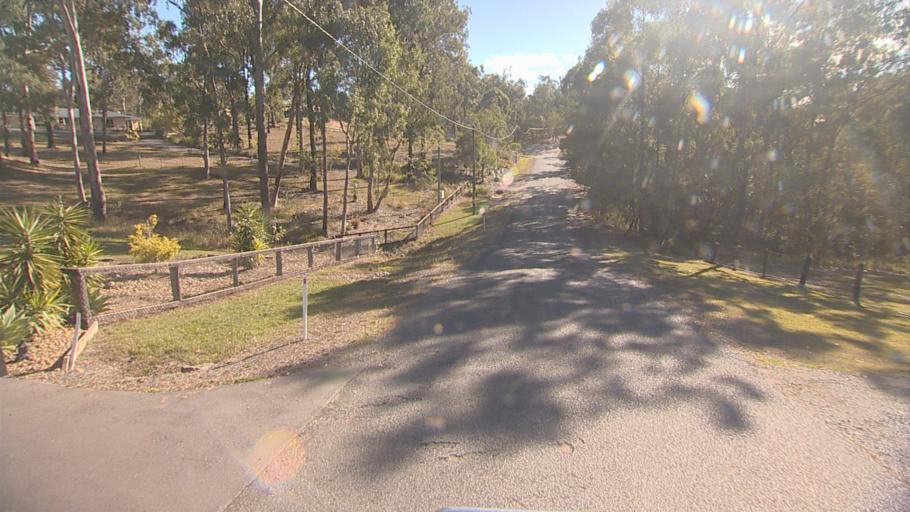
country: AU
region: Queensland
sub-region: Ipswich
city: Springfield Lakes
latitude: -27.7006
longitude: 152.9263
